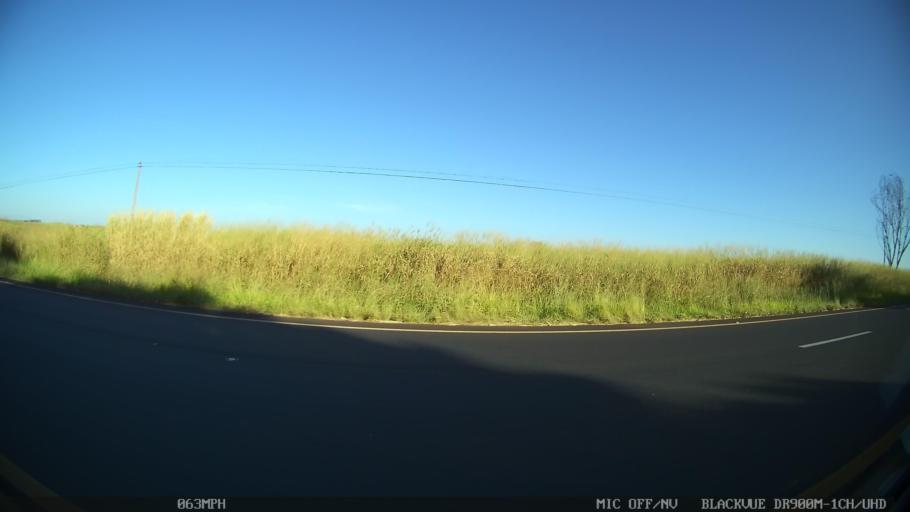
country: BR
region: Sao Paulo
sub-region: Olimpia
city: Olimpia
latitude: -20.7261
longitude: -49.0373
